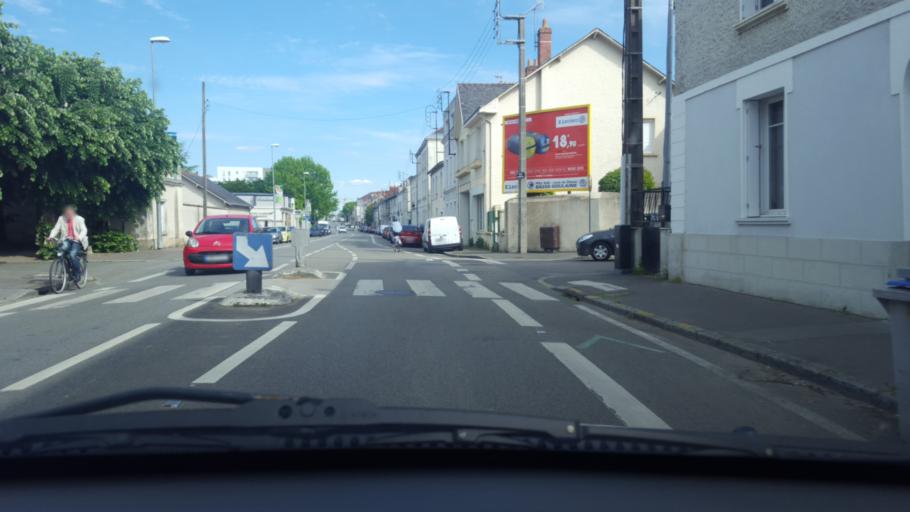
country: FR
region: Pays de la Loire
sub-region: Departement de la Loire-Atlantique
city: Reze
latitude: 47.1952
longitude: -1.5348
